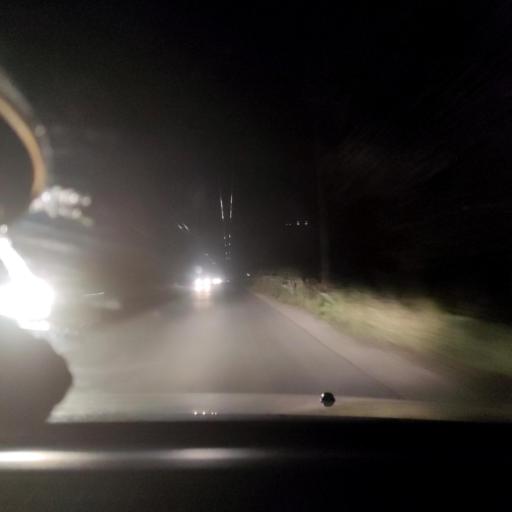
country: RU
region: Samara
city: Novokuybyshevsk
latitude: 53.0729
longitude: 49.8888
